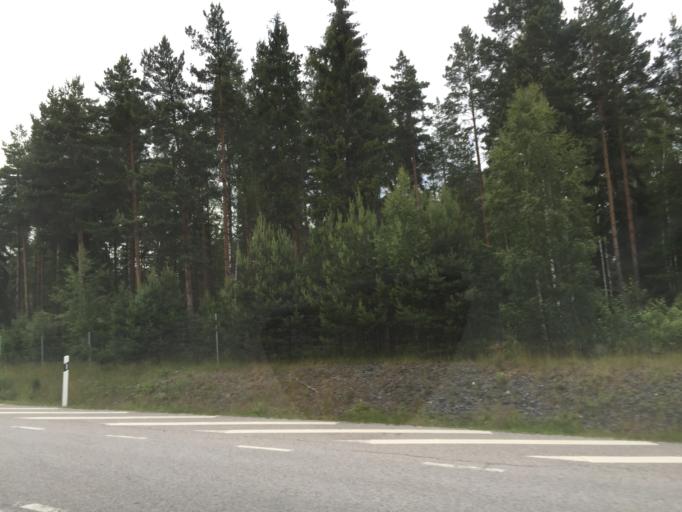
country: SE
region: OErebro
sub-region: Lindesbergs Kommun
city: Fellingsbro
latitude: 59.3379
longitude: 15.5478
